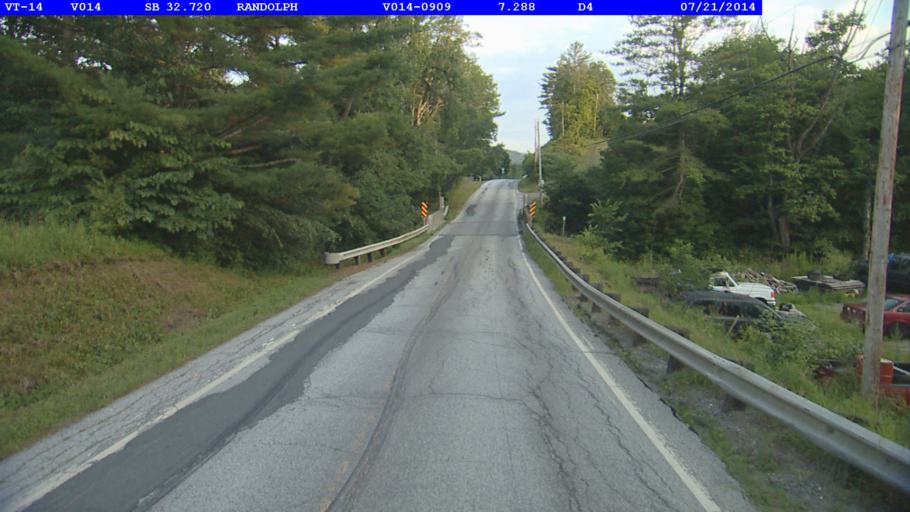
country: US
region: Vermont
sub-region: Orange County
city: Chelsea
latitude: 43.9728
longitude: -72.5549
